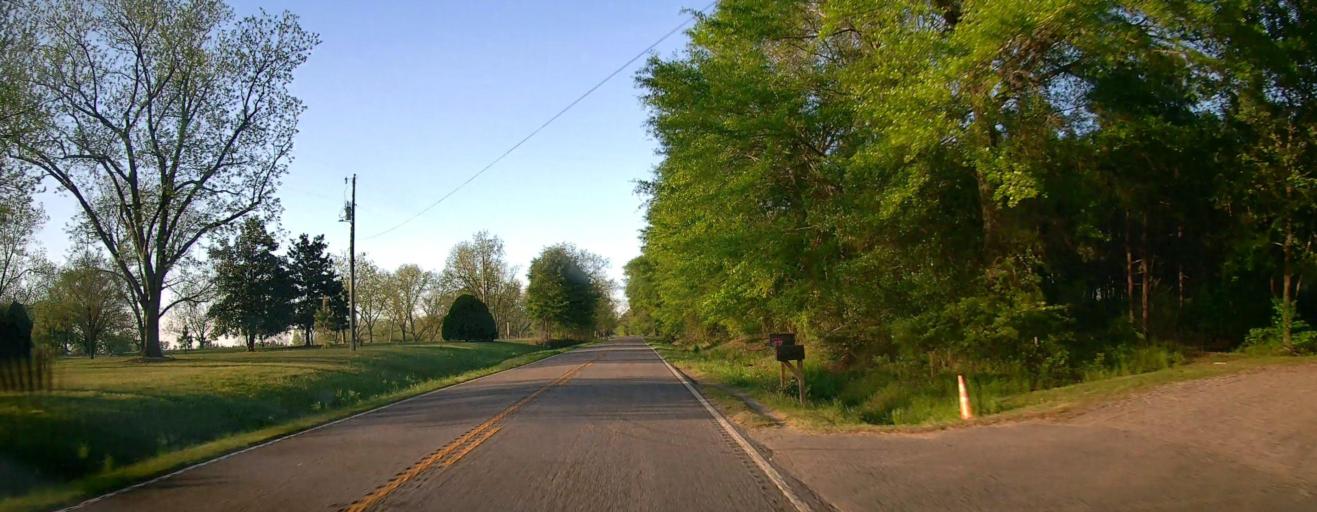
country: US
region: Georgia
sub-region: Marion County
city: Buena Vista
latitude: 32.4071
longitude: -84.4384
